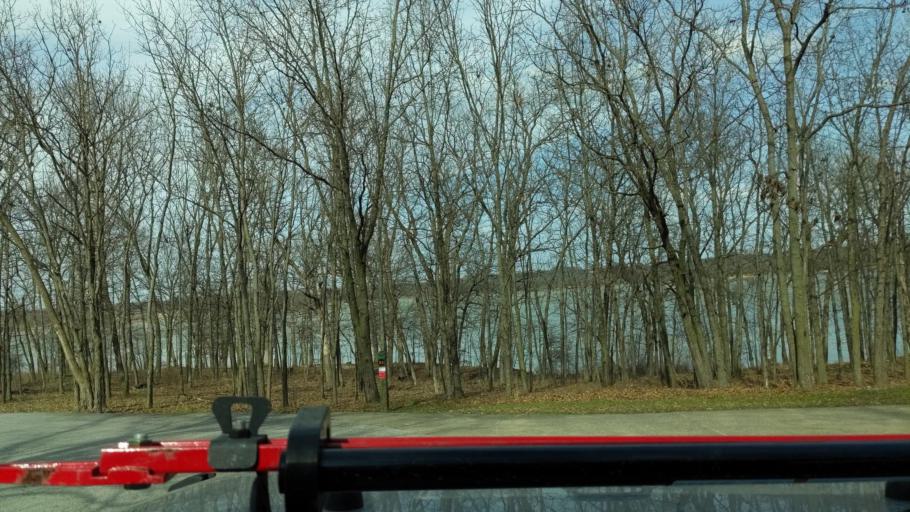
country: US
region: Missouri
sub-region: Macon County
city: Macon
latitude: 39.7694
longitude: -92.5181
